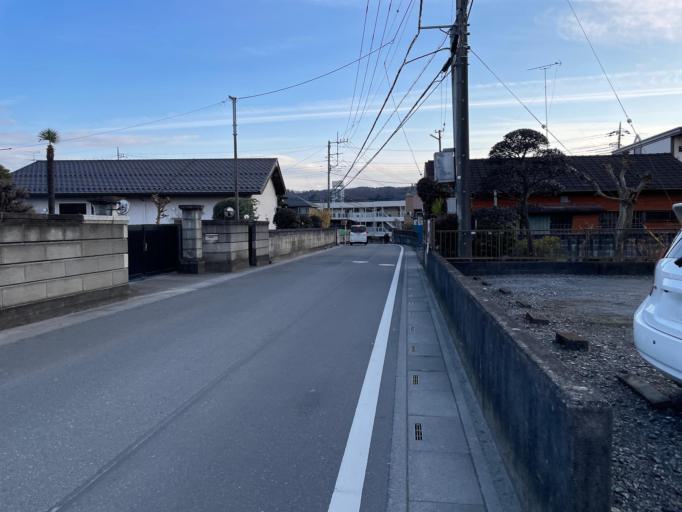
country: JP
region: Saitama
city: Hanno
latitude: 35.8417
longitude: 139.3476
